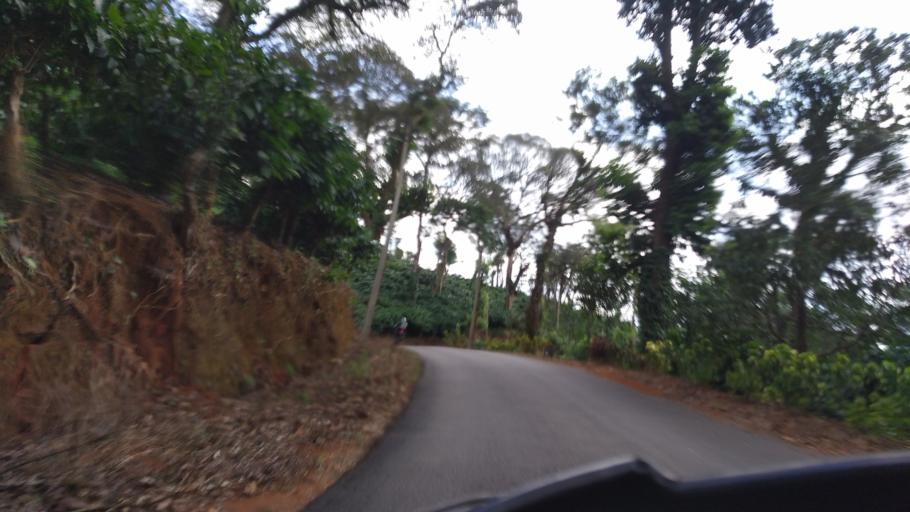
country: IN
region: Karnataka
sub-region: Kodagu
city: Ponnampet
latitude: 12.0330
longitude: 75.9206
